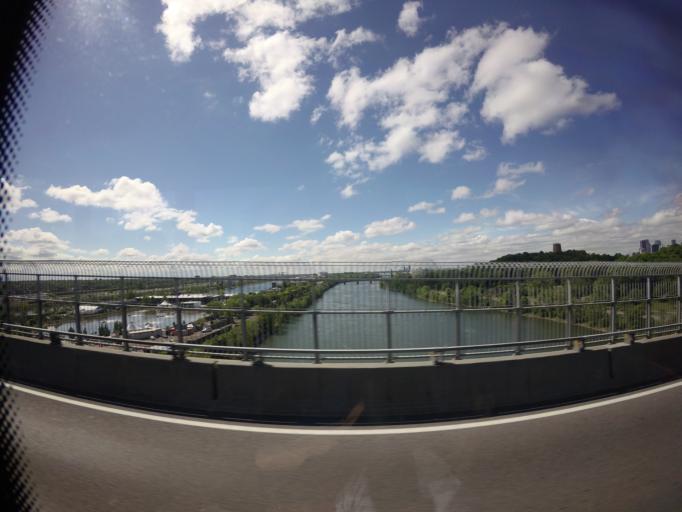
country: CA
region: Quebec
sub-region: Monteregie
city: Longueuil
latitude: 45.5211
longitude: -73.5293
